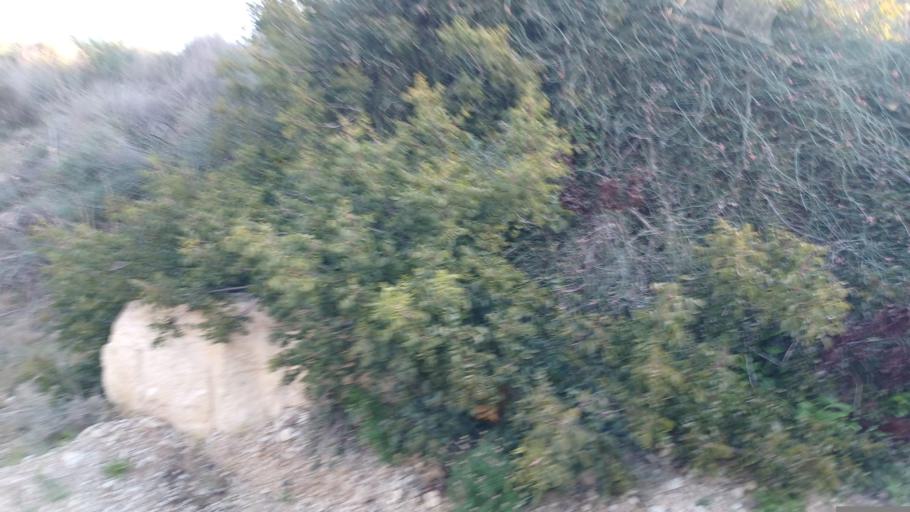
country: CY
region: Pafos
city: Kissonerga
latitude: 34.8341
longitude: 32.3964
